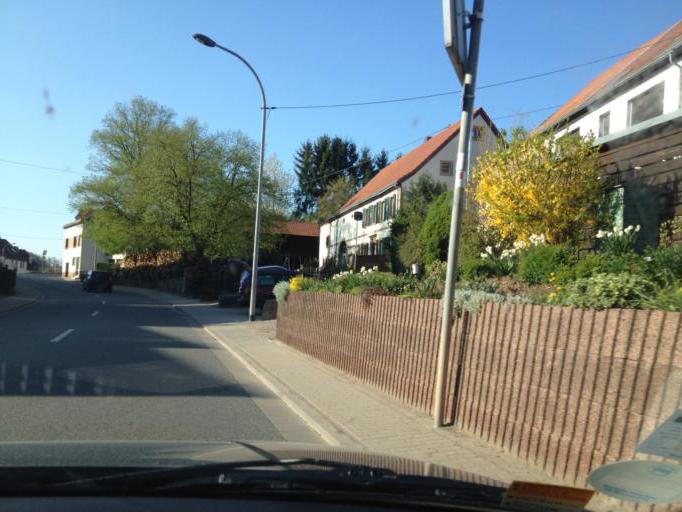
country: DE
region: Saarland
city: Sankt Wendel
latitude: 49.4776
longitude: 7.1773
